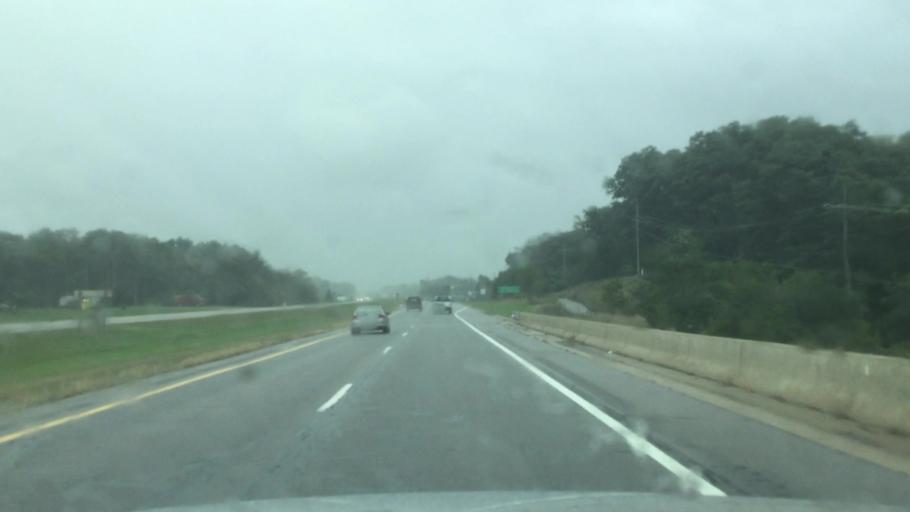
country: US
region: Michigan
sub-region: Livingston County
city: Howell
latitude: 42.6218
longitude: -83.9647
